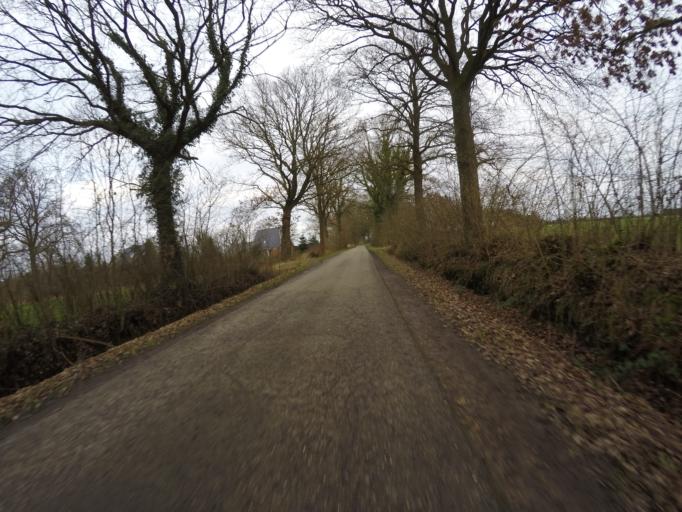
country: DE
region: Schleswig-Holstein
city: Alveslohe
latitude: 53.7995
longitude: 9.9045
